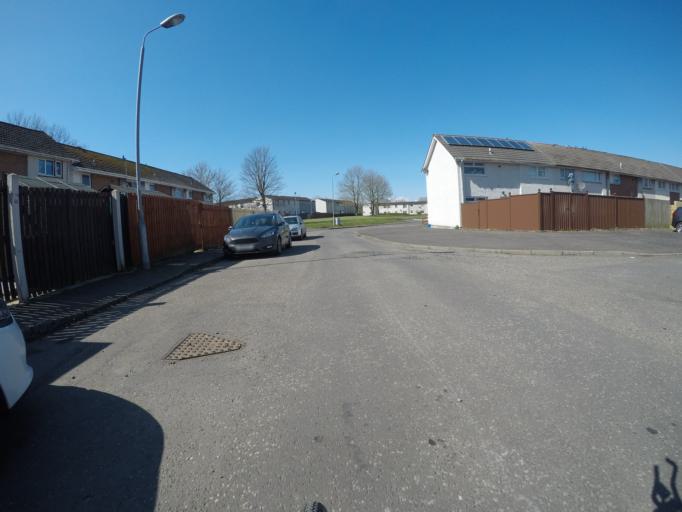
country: GB
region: Scotland
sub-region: North Ayrshire
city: Irvine
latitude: 55.6297
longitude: -4.6588
